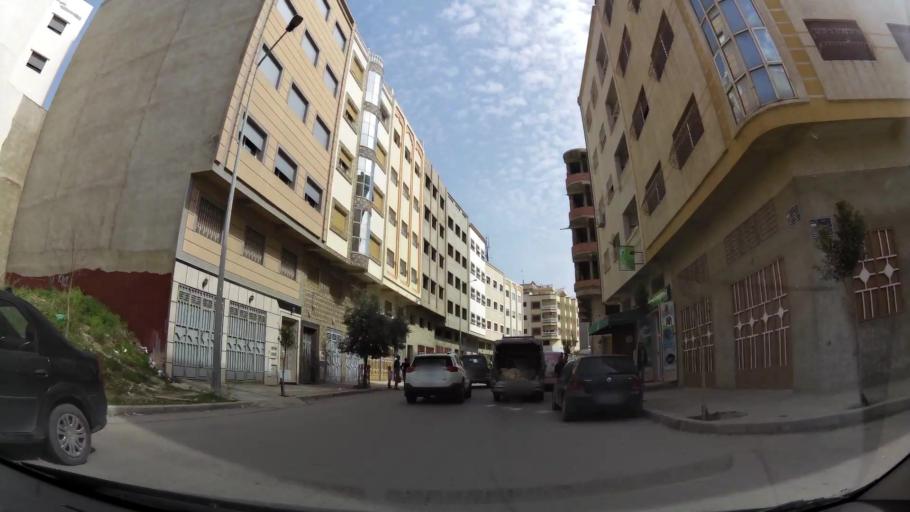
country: MA
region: Tanger-Tetouan
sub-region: Tanger-Assilah
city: Tangier
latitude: 35.7430
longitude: -5.8345
